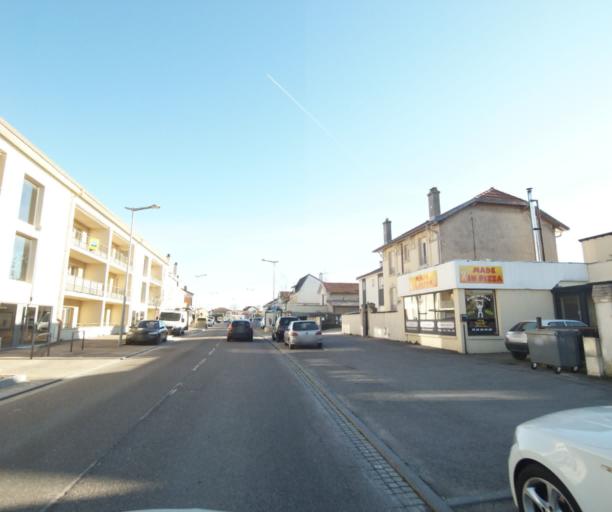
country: FR
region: Lorraine
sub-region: Departement de Meurthe-et-Moselle
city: Laneuveville-devant-Nancy
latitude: 48.6532
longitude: 6.2331
